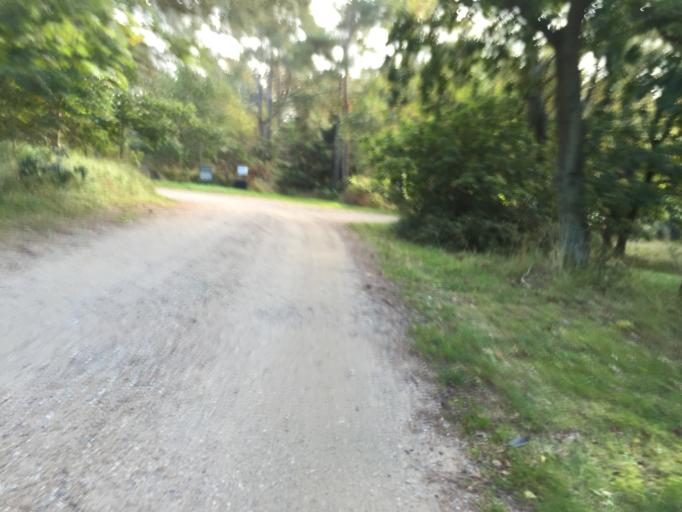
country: DK
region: Zealand
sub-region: Odsherred Kommune
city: Hojby
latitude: 55.9012
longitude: 11.5544
